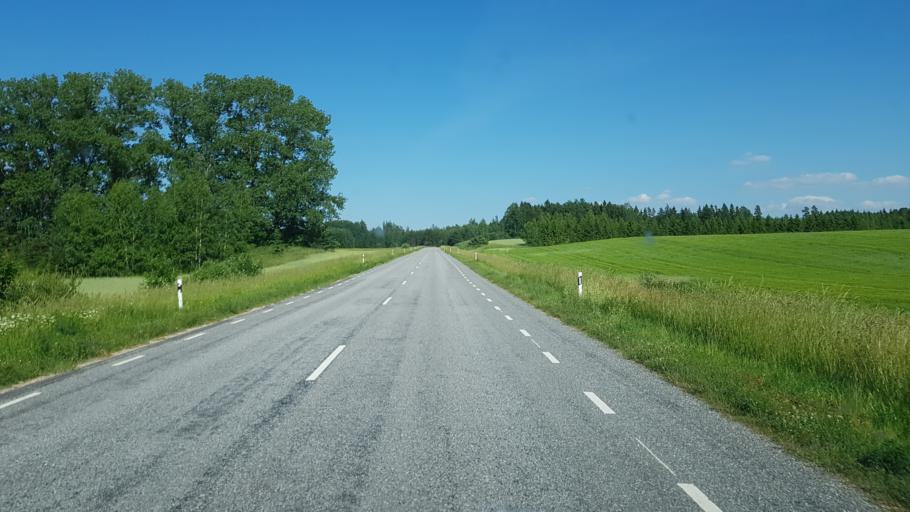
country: EE
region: Vorumaa
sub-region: Voru linn
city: Voru
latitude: 57.8579
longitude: 27.2236
